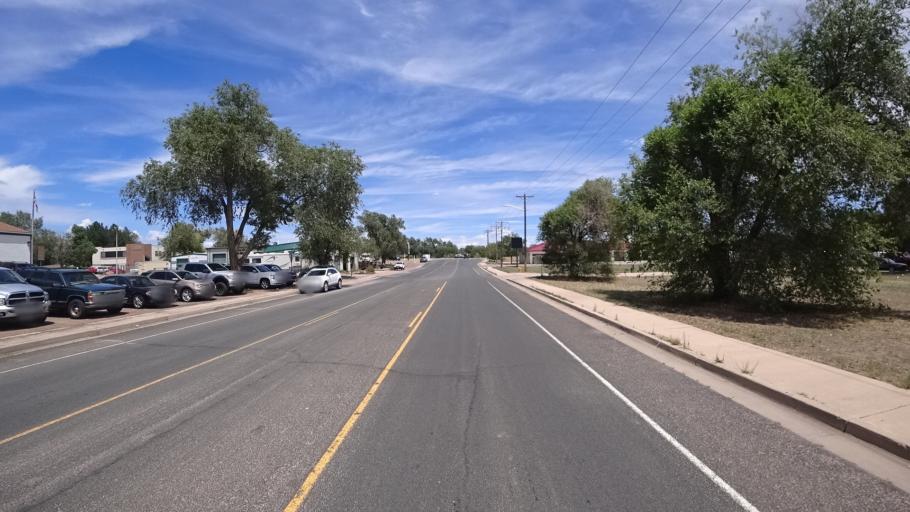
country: US
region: Colorado
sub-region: El Paso County
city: Security-Widefield
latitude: 38.7315
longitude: -104.7283
